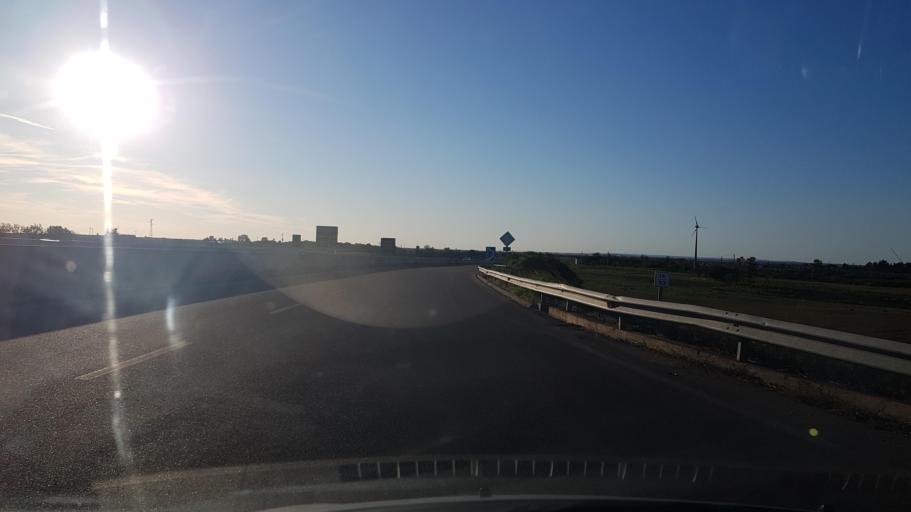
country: IT
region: Apulia
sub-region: Provincia di Brindisi
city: San Pancrazio Salentino
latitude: 40.4083
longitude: 17.8295
